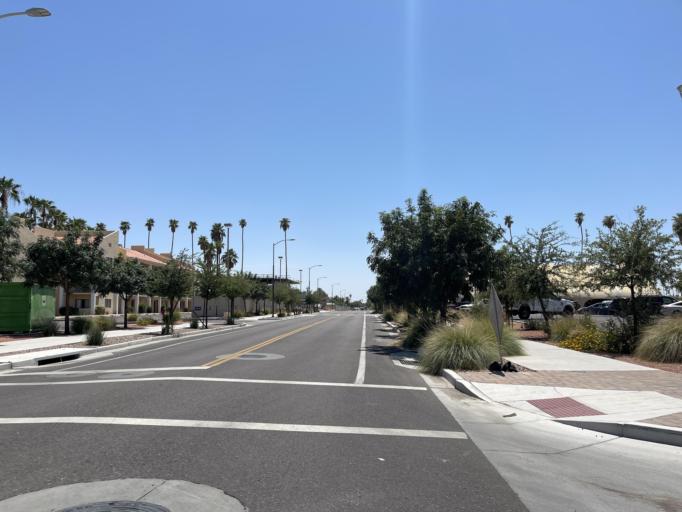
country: US
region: Arizona
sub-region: Maricopa County
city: Chandler
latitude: 33.3046
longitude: -111.8453
